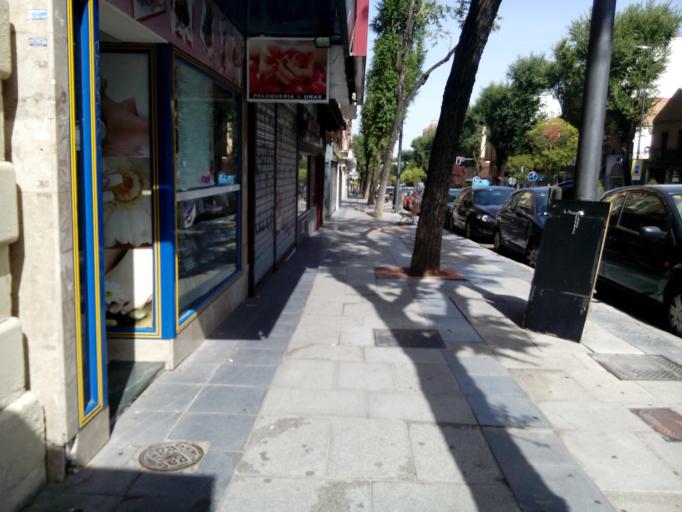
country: ES
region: Madrid
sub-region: Provincia de Madrid
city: Latina
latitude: 40.4100
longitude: -3.7376
